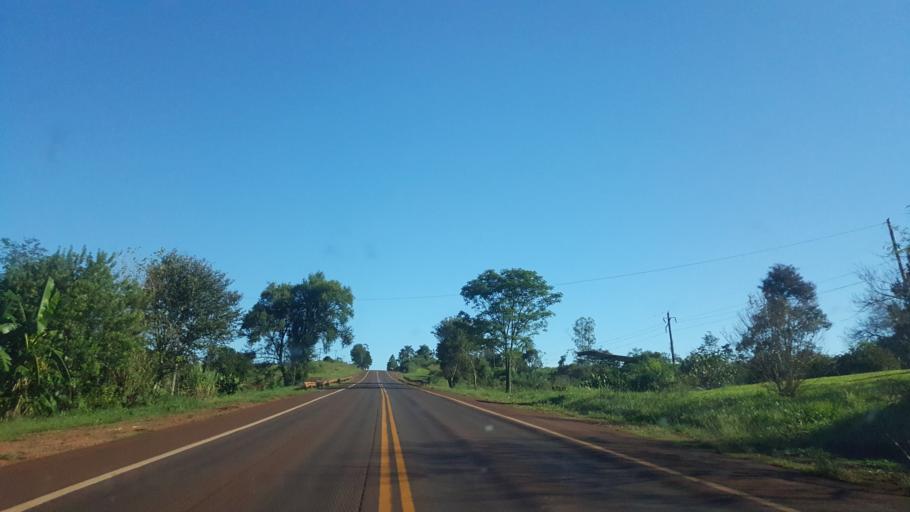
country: AR
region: Misiones
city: Puerto Esperanza
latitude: -26.1426
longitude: -54.5824
